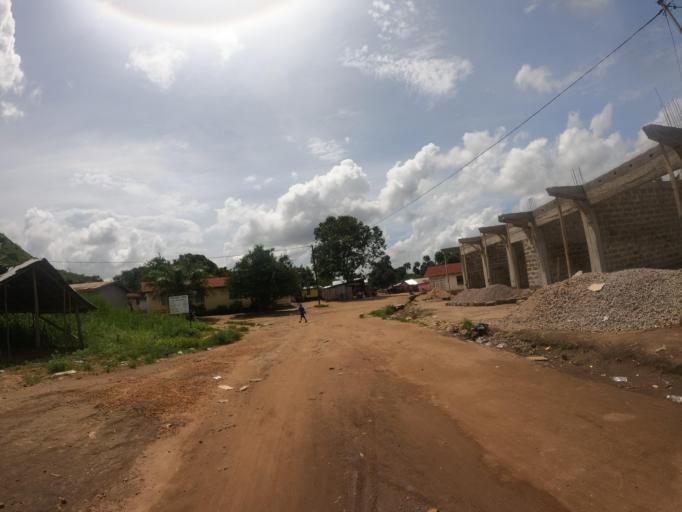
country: SL
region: Northern Province
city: Makeni
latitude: 8.9015
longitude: -12.0568
